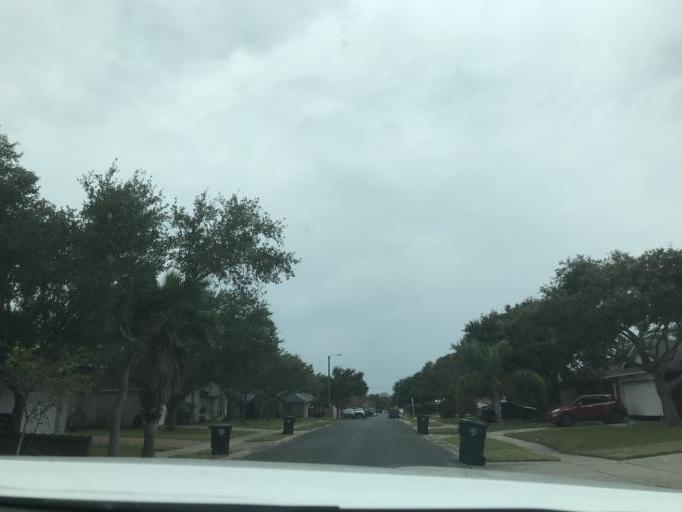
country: US
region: Texas
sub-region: Nueces County
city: Corpus Christi
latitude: 27.6705
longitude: -97.3462
